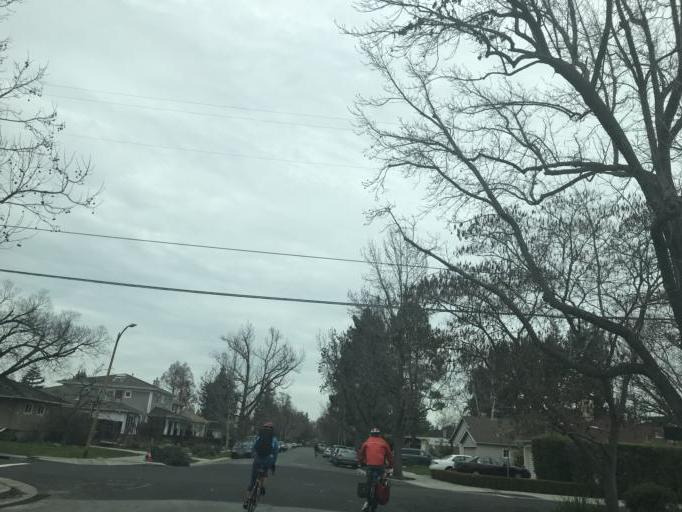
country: US
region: California
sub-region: Santa Clara County
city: Palo Alto
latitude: 37.4275
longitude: -122.1330
